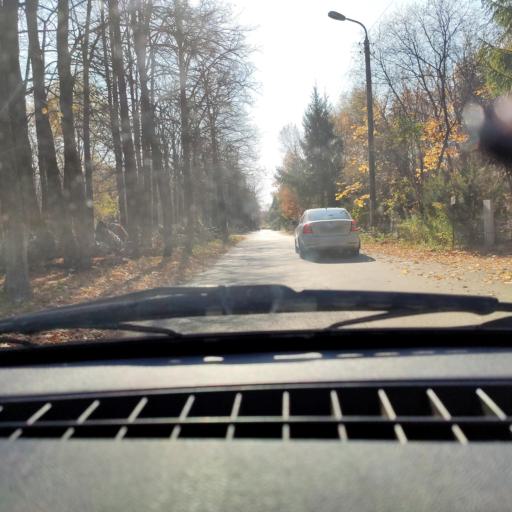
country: RU
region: Bashkortostan
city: Mikhaylovka
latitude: 54.8098
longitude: 55.8631
